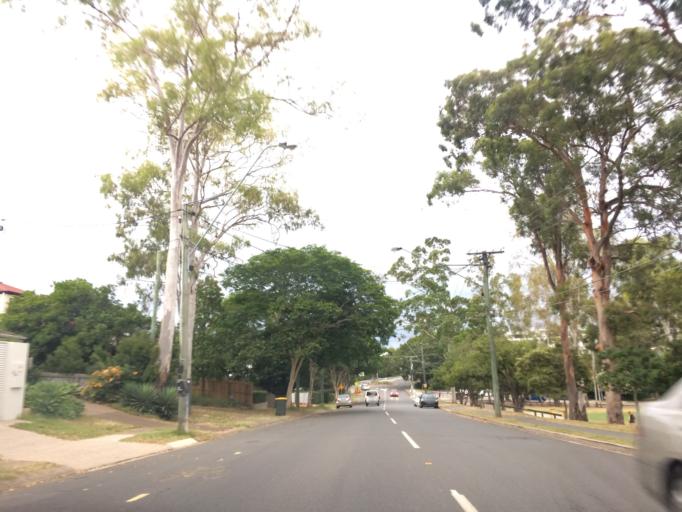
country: AU
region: Queensland
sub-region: Brisbane
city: Taringa
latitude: -27.5030
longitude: 152.9820
